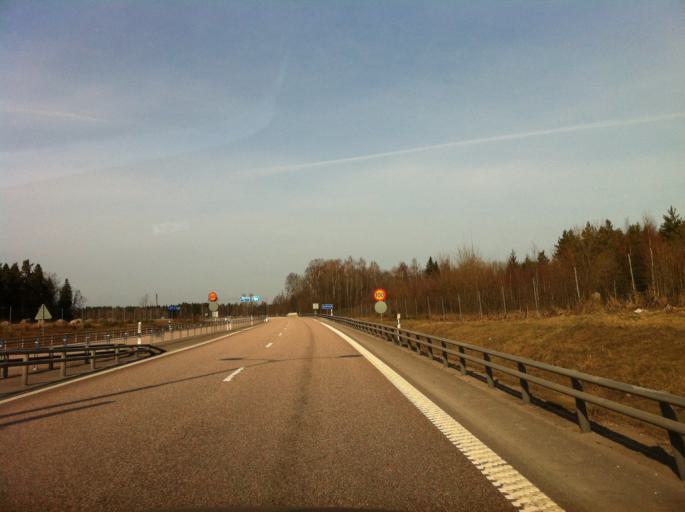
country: SE
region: Vaestra Goetaland
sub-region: Skovde Kommun
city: Skultorp
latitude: 58.3576
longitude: 13.8657
